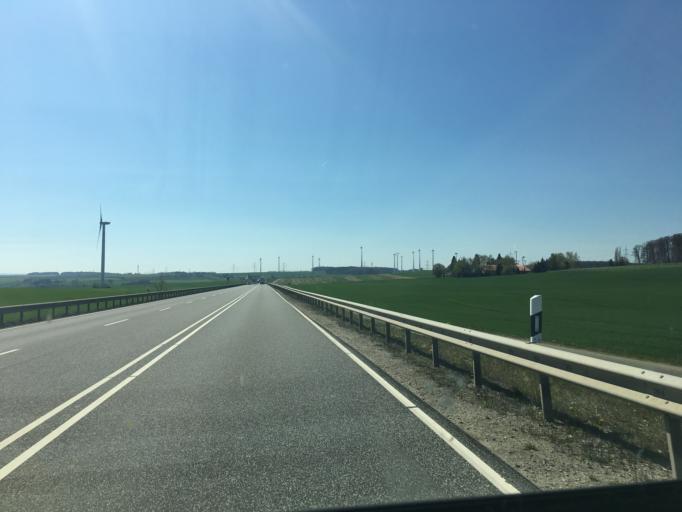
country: DE
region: Rheinland-Pfalz
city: Idesheim
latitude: 49.8730
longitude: 6.5447
